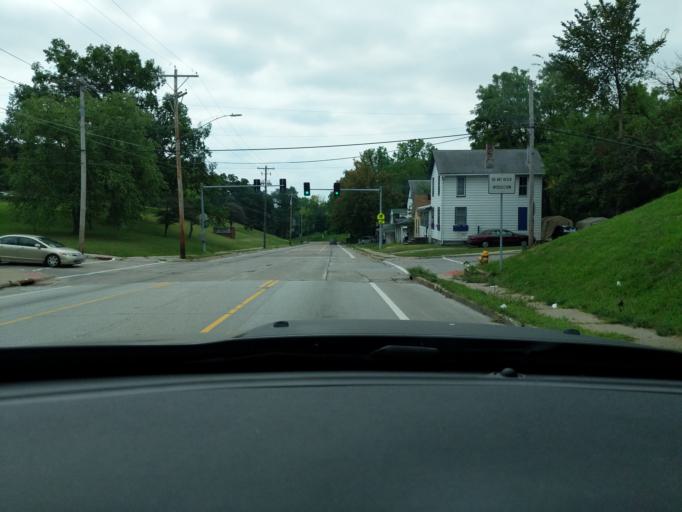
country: US
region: Iowa
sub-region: Scott County
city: Davenport
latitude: 41.5319
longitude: -90.5915
